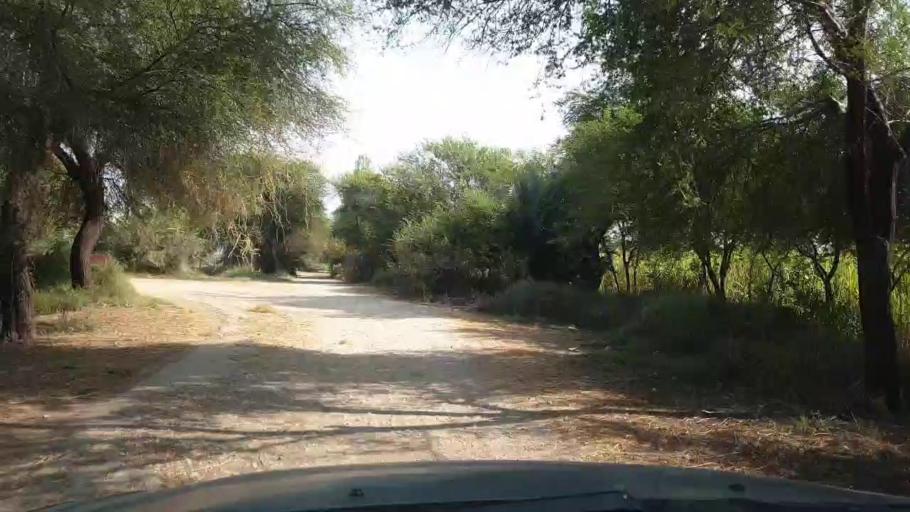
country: PK
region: Sindh
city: Bulri
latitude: 24.9048
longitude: 68.3754
